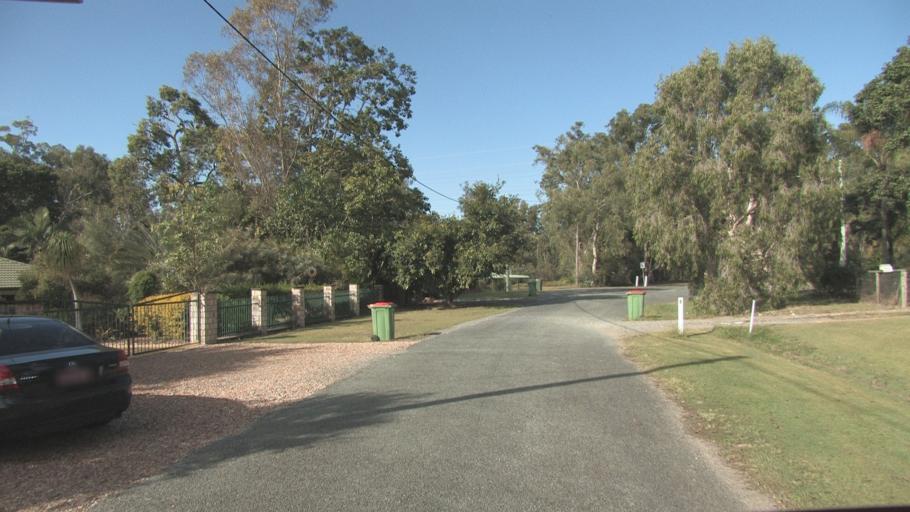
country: AU
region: Queensland
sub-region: Logan
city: Park Ridge South
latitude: -27.7339
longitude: 153.0349
